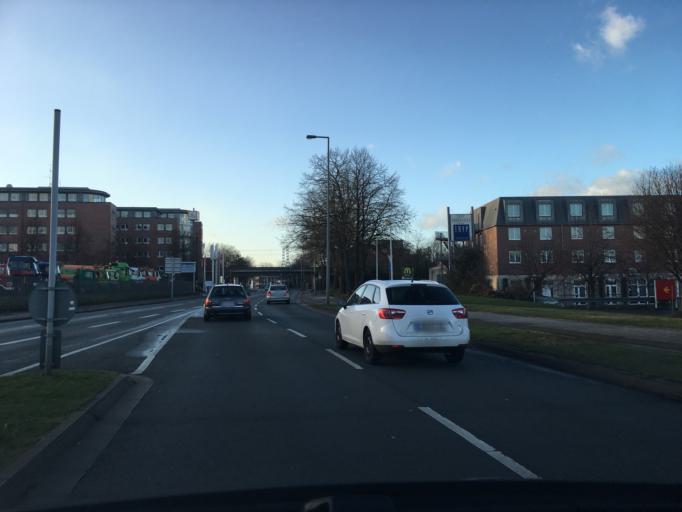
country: DE
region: North Rhine-Westphalia
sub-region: Regierungsbezirk Dusseldorf
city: Oberhausen
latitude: 51.4869
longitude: 6.8760
